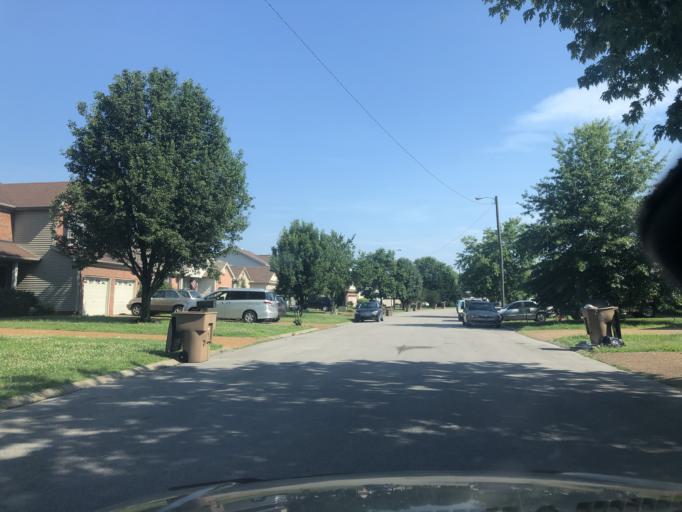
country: US
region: Tennessee
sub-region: Davidson County
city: Lakewood
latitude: 36.2381
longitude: -86.6979
